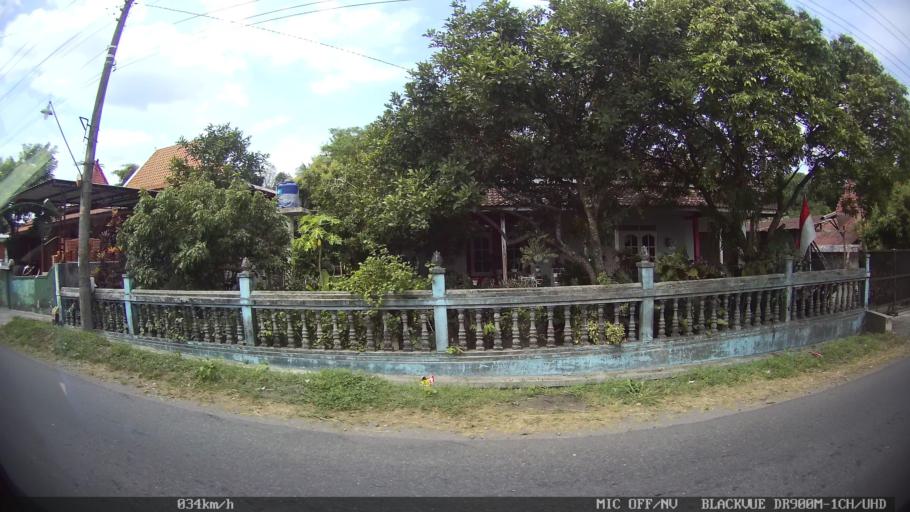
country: ID
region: Central Java
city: Candi Prambanan
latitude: -7.7312
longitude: 110.4722
